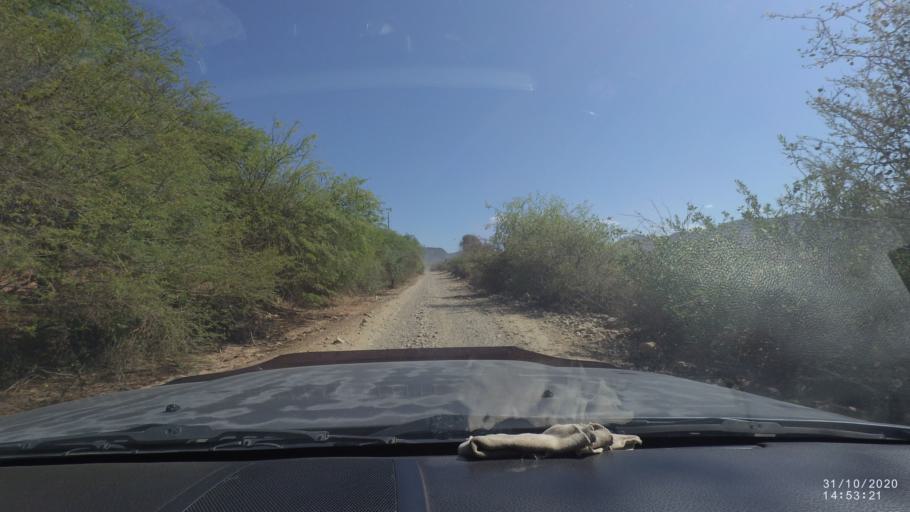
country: BO
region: Cochabamba
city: Aiquile
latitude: -18.2184
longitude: -64.8572
